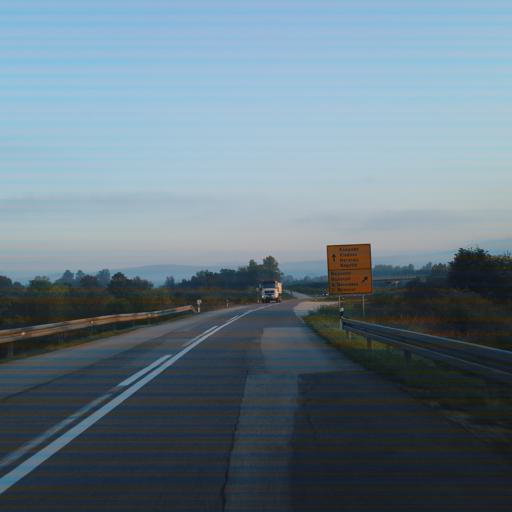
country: RS
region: Central Serbia
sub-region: Zajecarski Okrug
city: Zajecar
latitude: 43.9752
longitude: 22.2918
